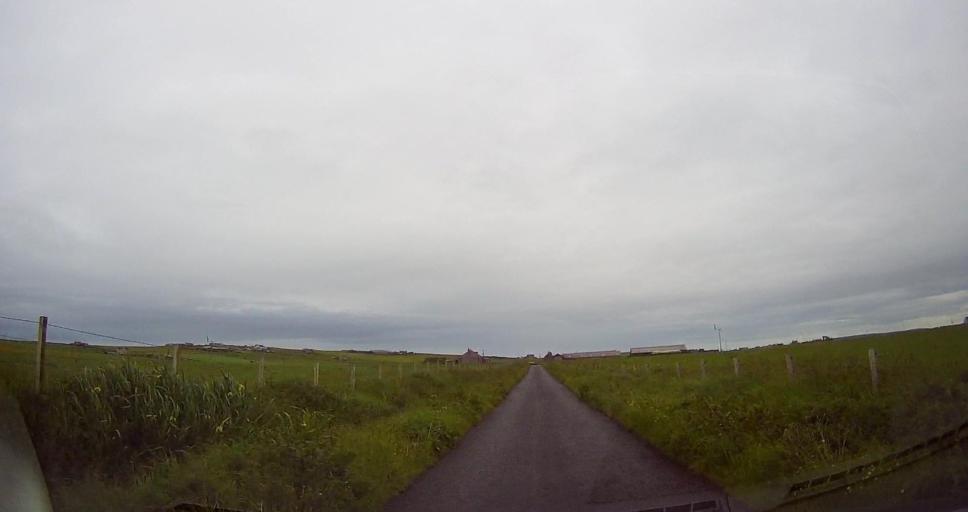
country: GB
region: Scotland
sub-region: Orkney Islands
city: Stromness
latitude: 59.1277
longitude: -3.2995
